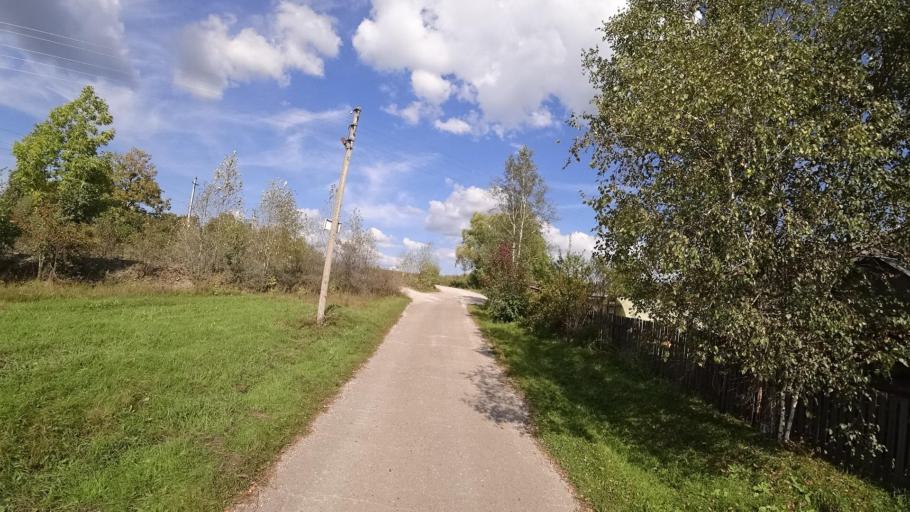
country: RU
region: Jewish Autonomous Oblast
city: Birakan
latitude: 49.0105
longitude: 131.7423
